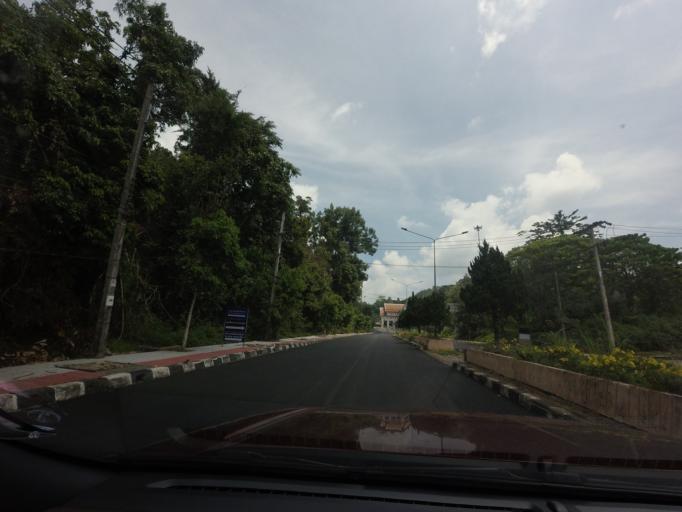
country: TH
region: Yala
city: Betong
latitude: 5.7477
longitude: 101.0333
